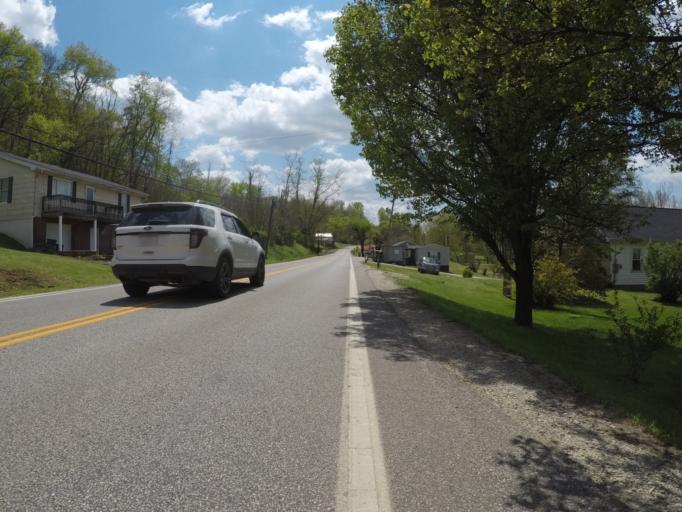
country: US
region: West Virginia
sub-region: Cabell County
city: Pea Ridge
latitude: 38.4546
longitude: -82.3755
